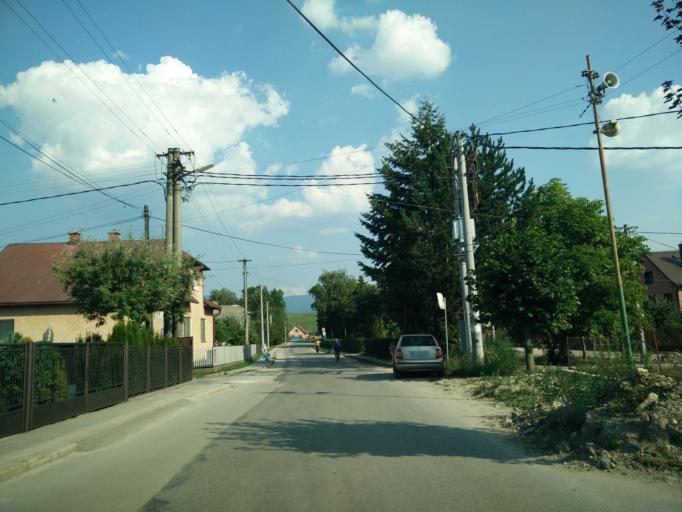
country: SK
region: Zilinsky
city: Rajec
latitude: 49.1199
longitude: 18.6494
